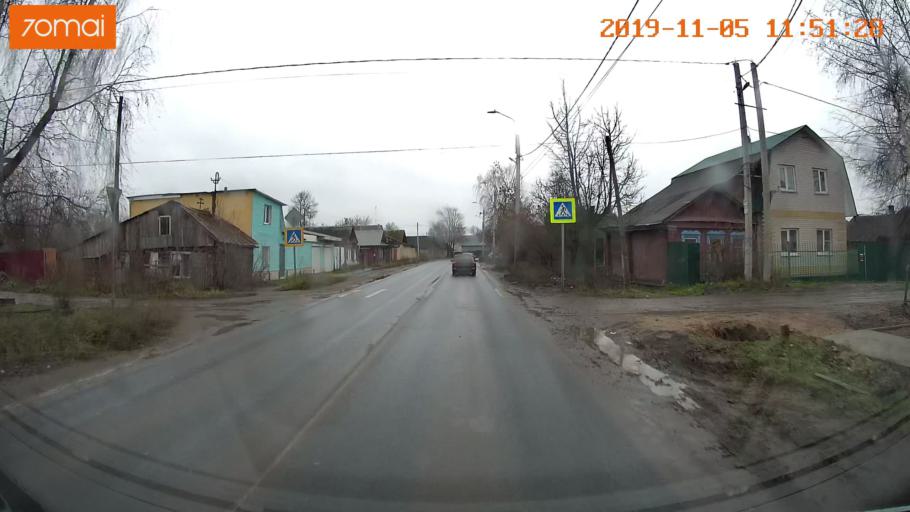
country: RU
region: Ivanovo
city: Bogorodskoye
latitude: 57.0055
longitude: 41.0275
